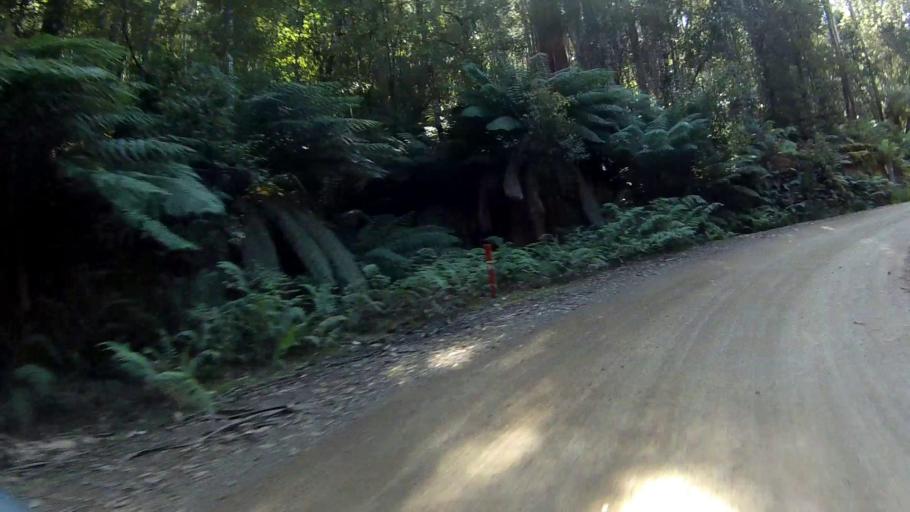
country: AU
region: Tasmania
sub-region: Derwent Valley
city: New Norfolk
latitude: -42.6783
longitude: 146.6989
